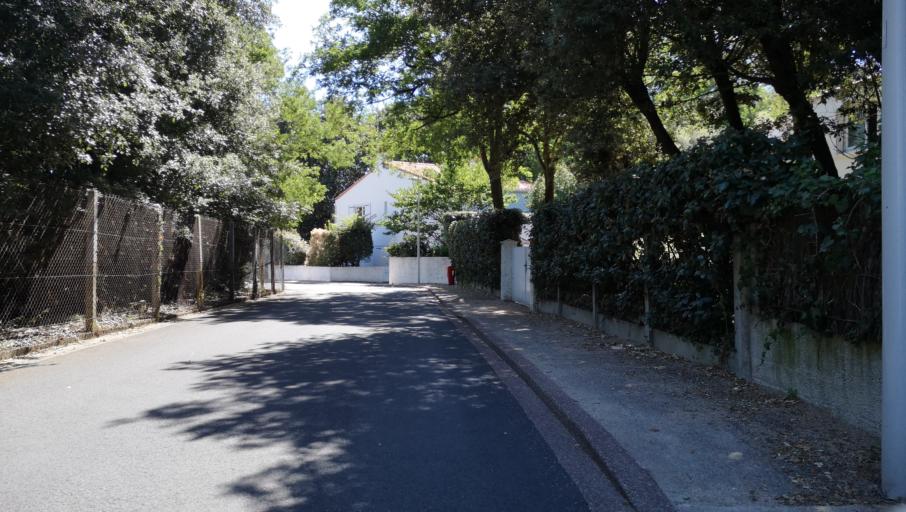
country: FR
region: Pays de la Loire
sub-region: Departement de la Vendee
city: Chateau-d'Olonne
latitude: 46.4791
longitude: -1.7520
